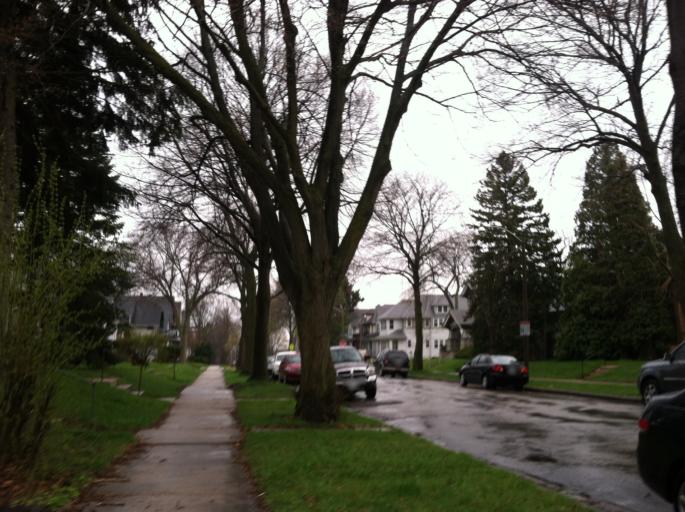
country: US
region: Wisconsin
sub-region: Milwaukee County
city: Shorewood
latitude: 43.0737
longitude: -87.8902
